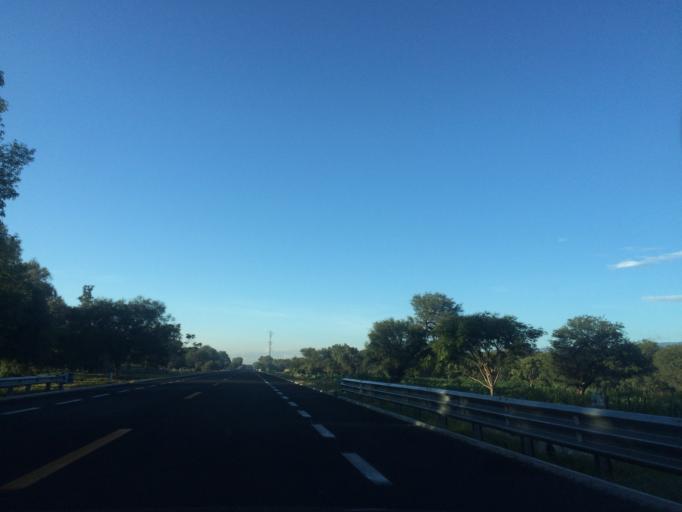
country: MX
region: Puebla
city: Santiago Miahuatlan
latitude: 18.5404
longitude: -97.4600
